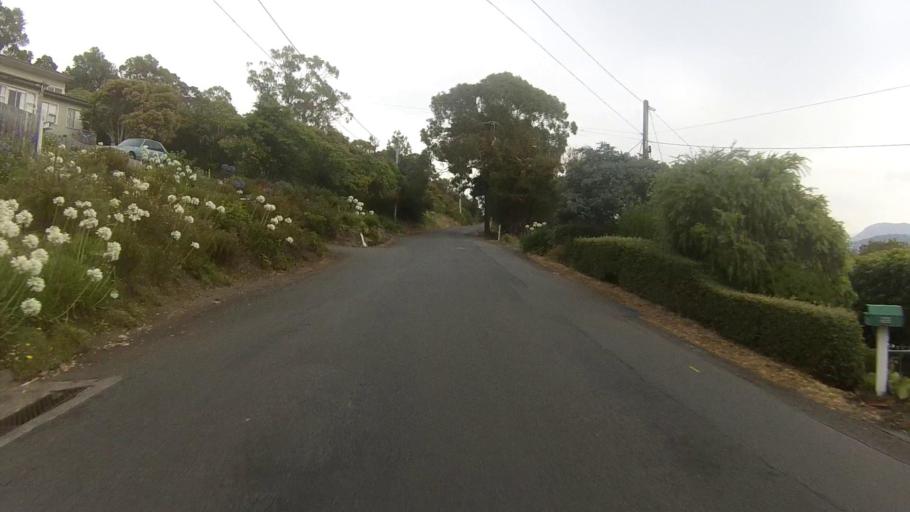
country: AU
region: Tasmania
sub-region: Hobart
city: Dynnyrne
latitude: -42.9090
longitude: 147.3273
